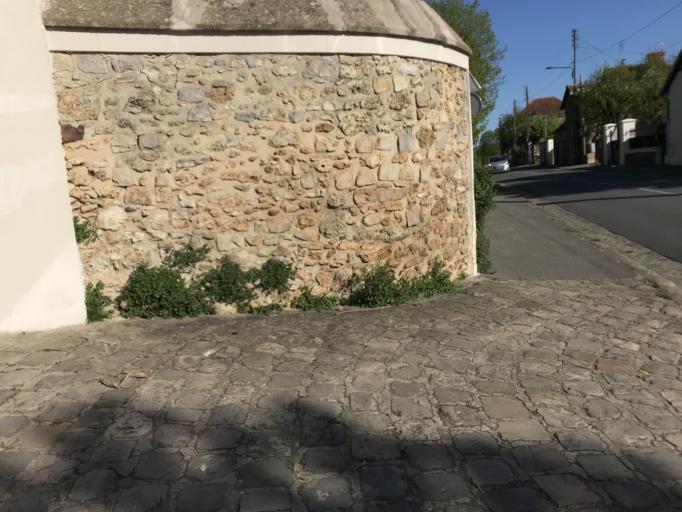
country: FR
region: Ile-de-France
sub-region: Departement de l'Essonne
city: Marcoussis
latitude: 48.6441
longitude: 2.2265
